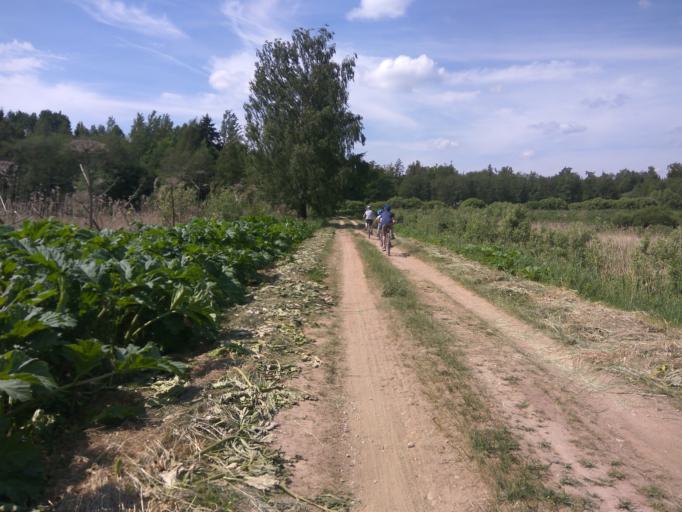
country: LV
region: Kuldigas Rajons
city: Kuldiga
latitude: 56.9303
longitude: 21.9749
